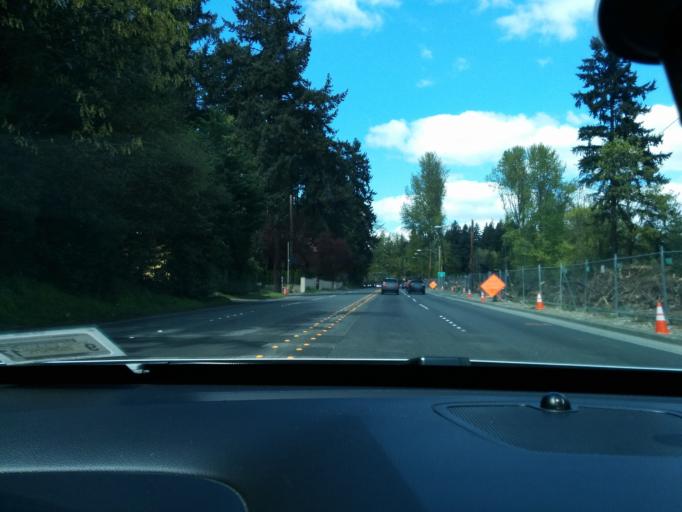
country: US
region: Washington
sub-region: King County
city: Bellevue
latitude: 47.5915
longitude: -122.1936
